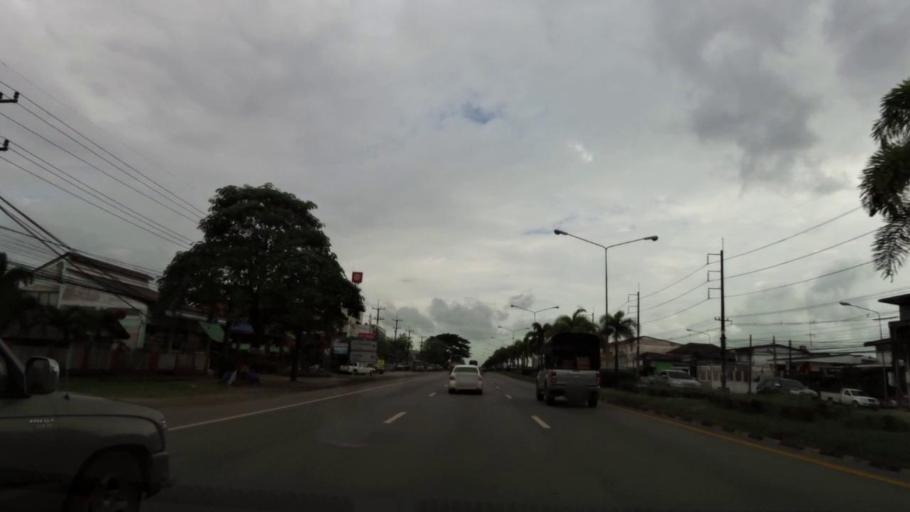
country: TH
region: Chanthaburi
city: Tha Mai
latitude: 12.7217
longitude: 101.9699
